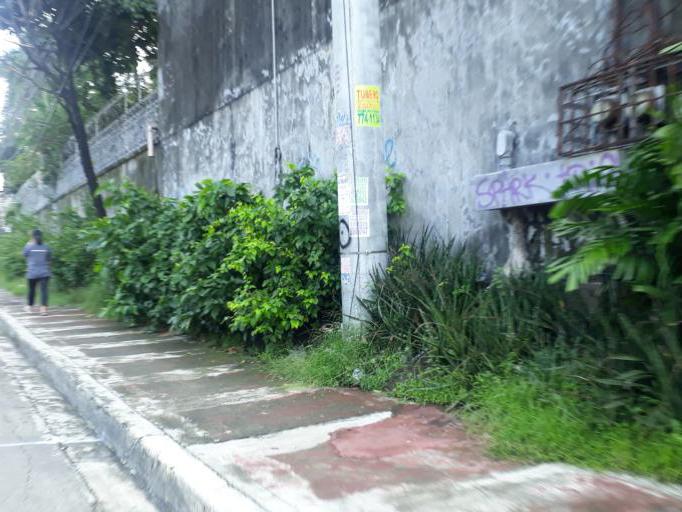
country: PH
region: Metro Manila
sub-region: San Juan
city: San Juan
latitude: 14.6202
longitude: 121.0250
